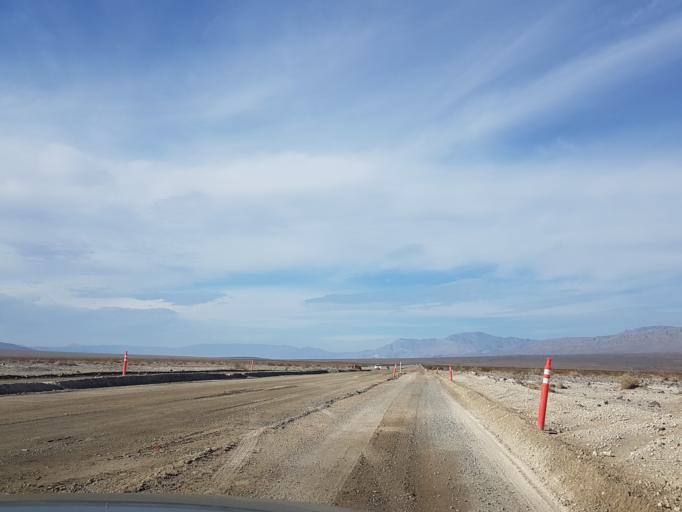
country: US
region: California
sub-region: San Bernardino County
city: Searles Valley
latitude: 36.1401
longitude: -117.2959
